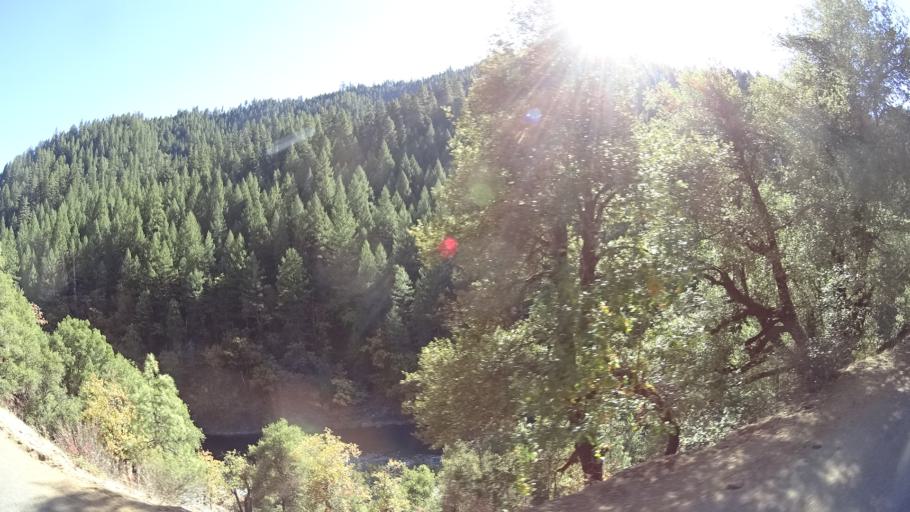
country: US
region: California
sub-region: Siskiyou County
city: Happy Camp
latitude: 41.3019
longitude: -123.1532
